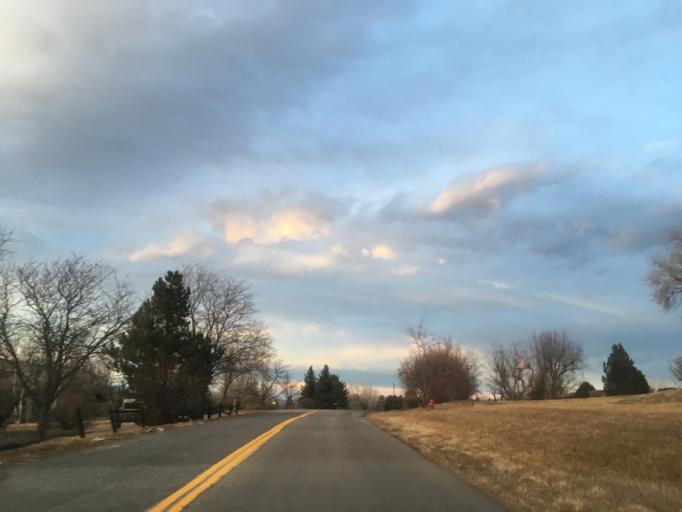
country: US
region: Colorado
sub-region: Boulder County
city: Superior
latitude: 39.9851
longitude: -105.1742
